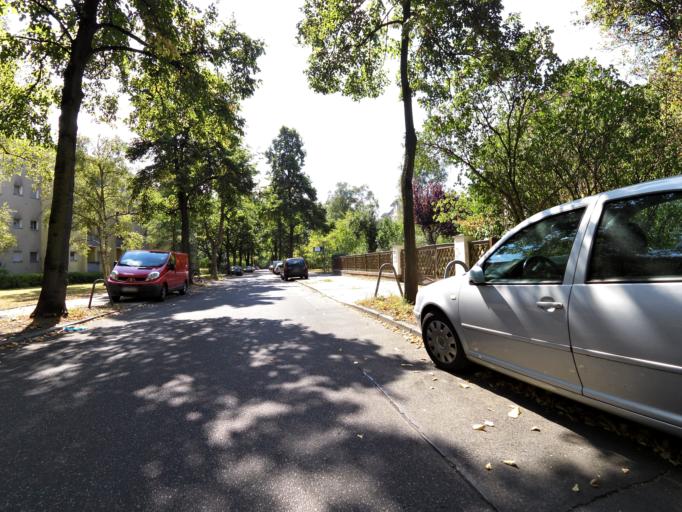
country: DE
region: Berlin
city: Lankwitz
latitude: 52.4482
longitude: 13.3494
